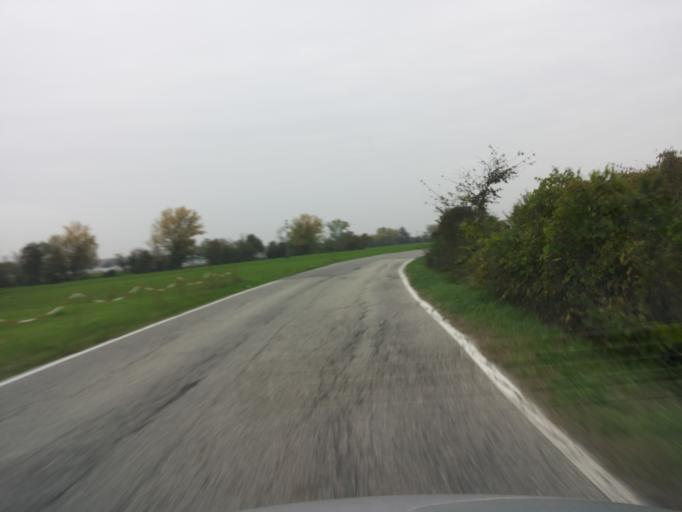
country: IT
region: Piedmont
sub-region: Provincia di Alessandria
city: San Giorgio Monferrato
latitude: 45.1043
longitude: 8.4370
